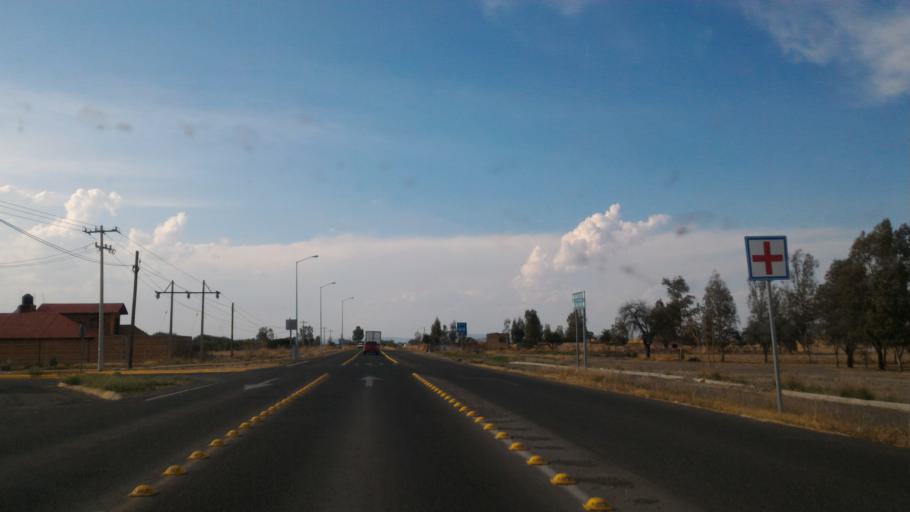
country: MX
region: Guanajuato
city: Ciudad Manuel Doblado
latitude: 20.7558
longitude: -101.9649
